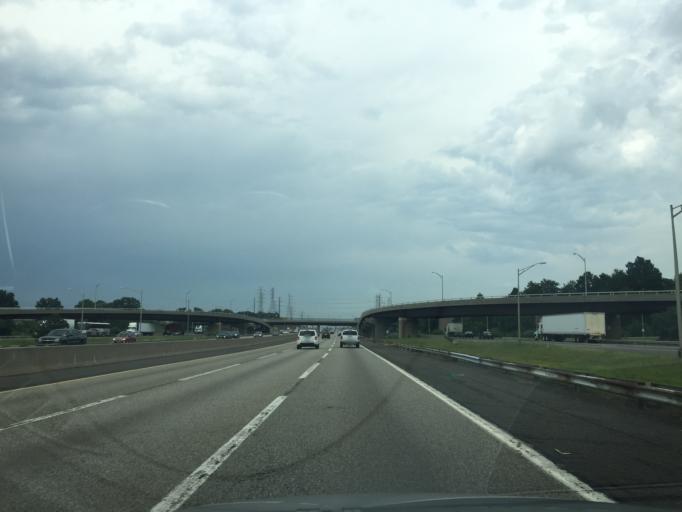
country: US
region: New Jersey
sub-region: Middlesex County
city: Port Reading
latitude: 40.5592
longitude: -74.2630
